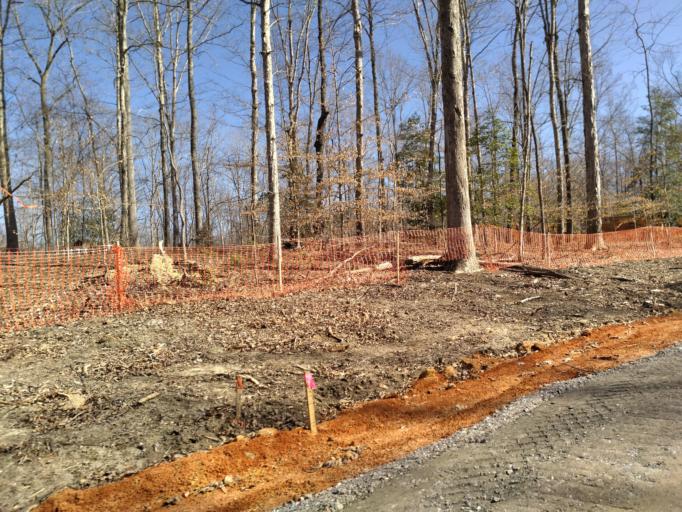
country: US
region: Virginia
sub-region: Chesterfield County
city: Chesterfield
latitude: 37.3829
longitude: -77.5586
